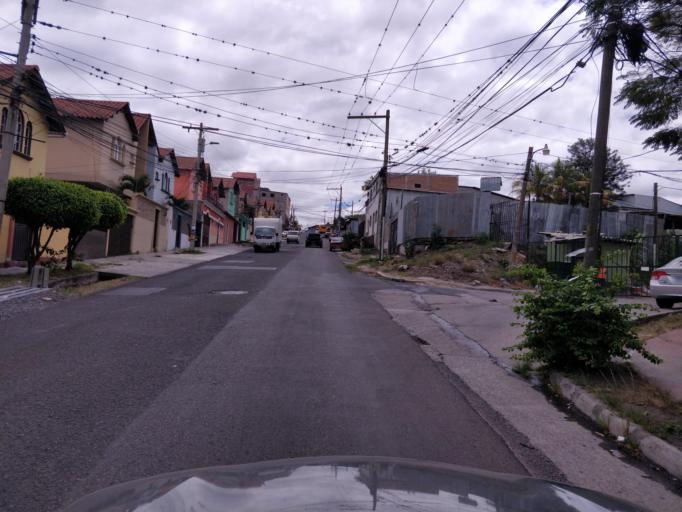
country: HN
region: Francisco Morazan
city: Tegucigalpa
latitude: 14.0511
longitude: -87.2182
